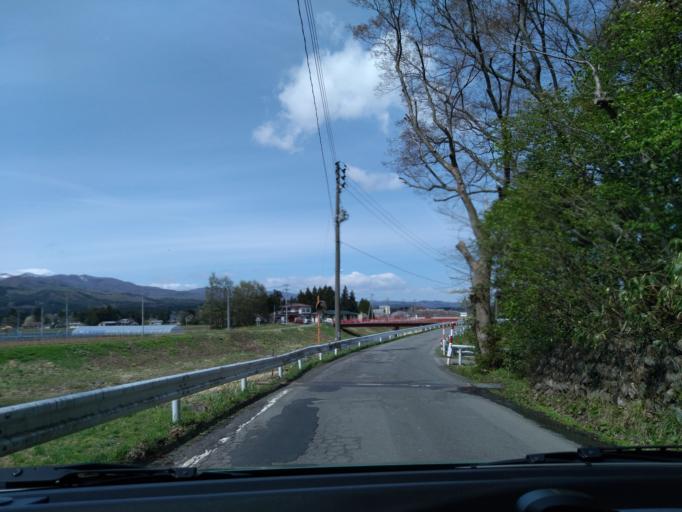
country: JP
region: Iwate
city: Kitakami
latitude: 39.2960
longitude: 140.9784
